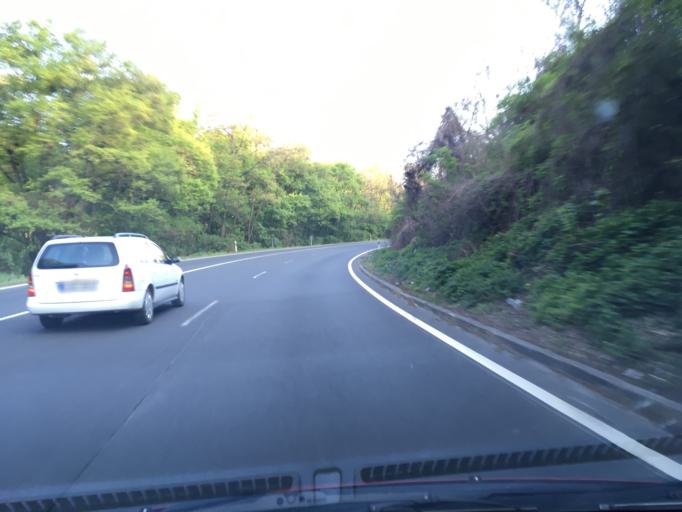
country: HU
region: Pest
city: Veroce
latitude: 47.8366
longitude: 19.0941
